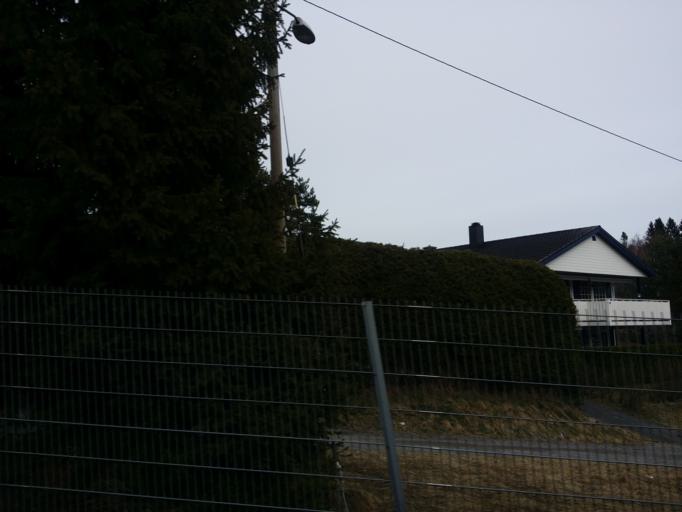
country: NO
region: Akershus
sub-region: Oppegard
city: Kolbotn
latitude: 59.8891
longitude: 10.8503
